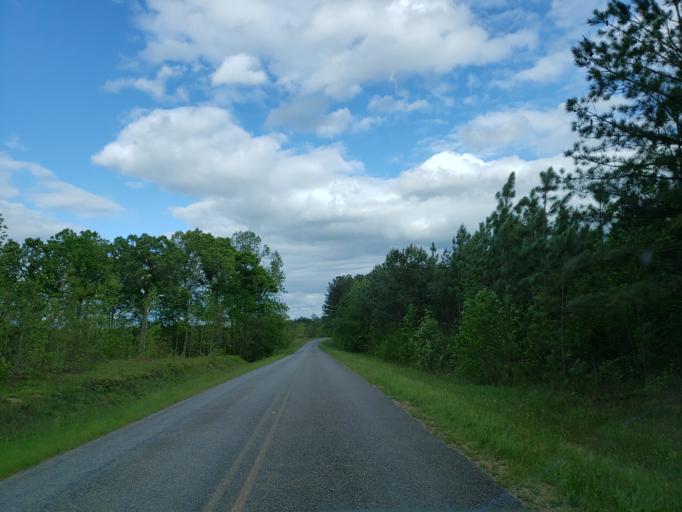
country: US
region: Georgia
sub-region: Haralson County
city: Tallapoosa
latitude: 33.8193
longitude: -85.3754
